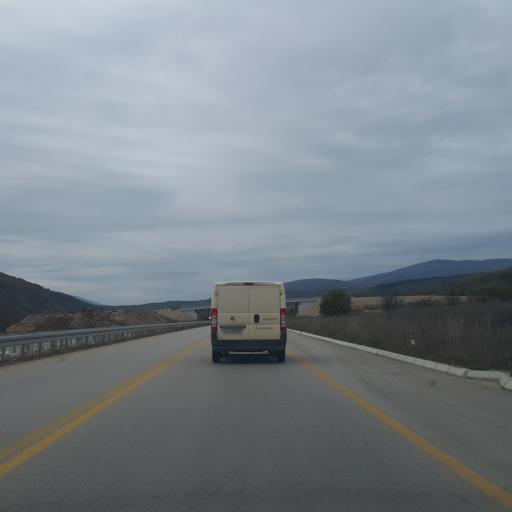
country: RS
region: Central Serbia
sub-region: Pirotski Okrug
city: Pirot
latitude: 43.2240
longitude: 22.4779
